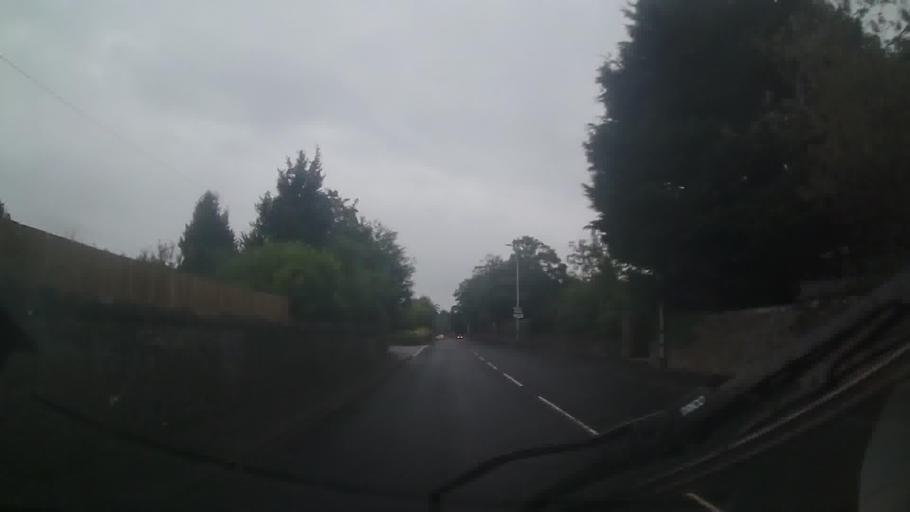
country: GB
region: Scotland
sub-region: North Ayrshire
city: Fairlie
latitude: 55.7535
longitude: -4.8553
